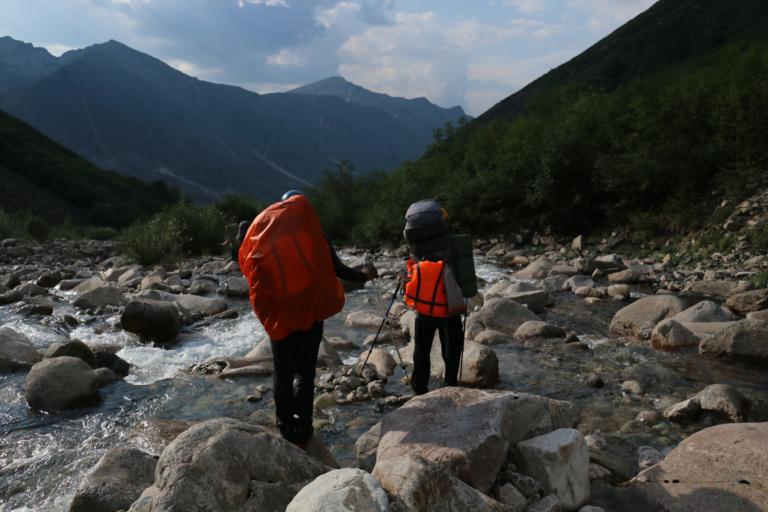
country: RU
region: Respublika Buryatiya
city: Novyy Uoyan
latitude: 56.3248
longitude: 111.1971
